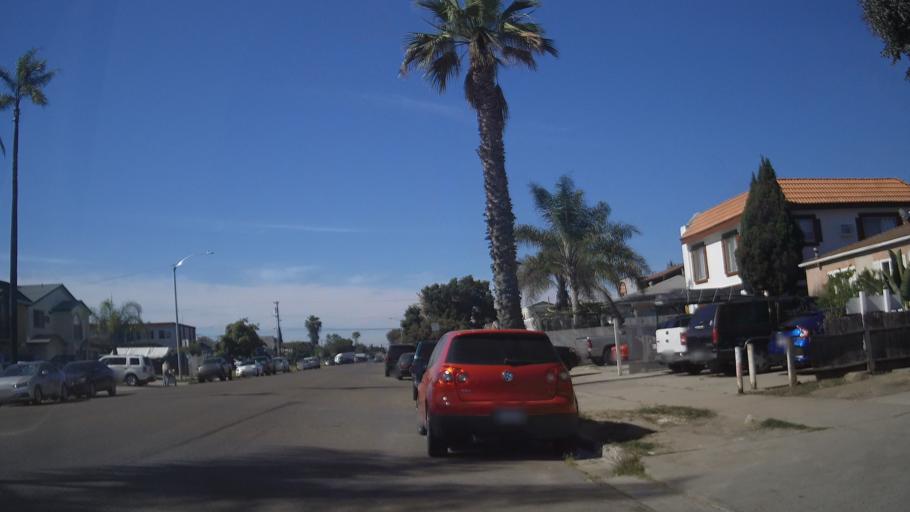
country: US
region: California
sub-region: San Diego County
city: San Diego
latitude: 32.7465
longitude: -117.1057
